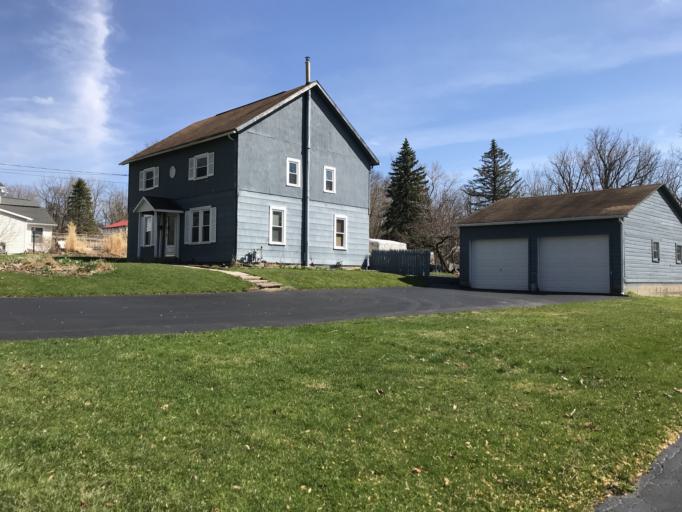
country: US
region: New York
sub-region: Livingston County
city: Geneseo
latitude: 42.7992
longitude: -77.8095
